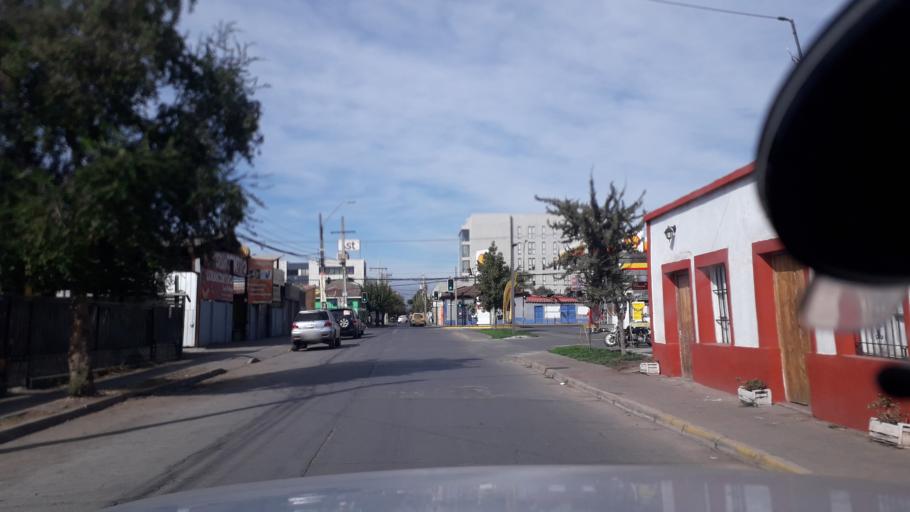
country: CL
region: Valparaiso
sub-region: Provincia de San Felipe
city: San Felipe
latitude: -32.7499
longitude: -70.7309
